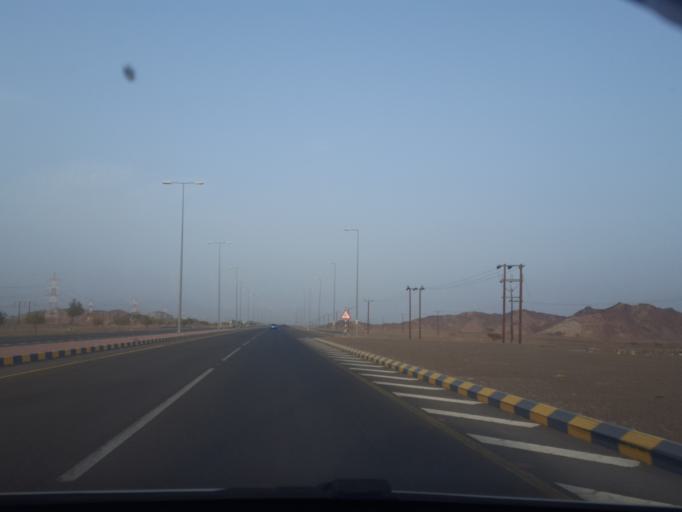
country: OM
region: Al Buraimi
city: Al Buraymi
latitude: 24.2463
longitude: 56.0038
